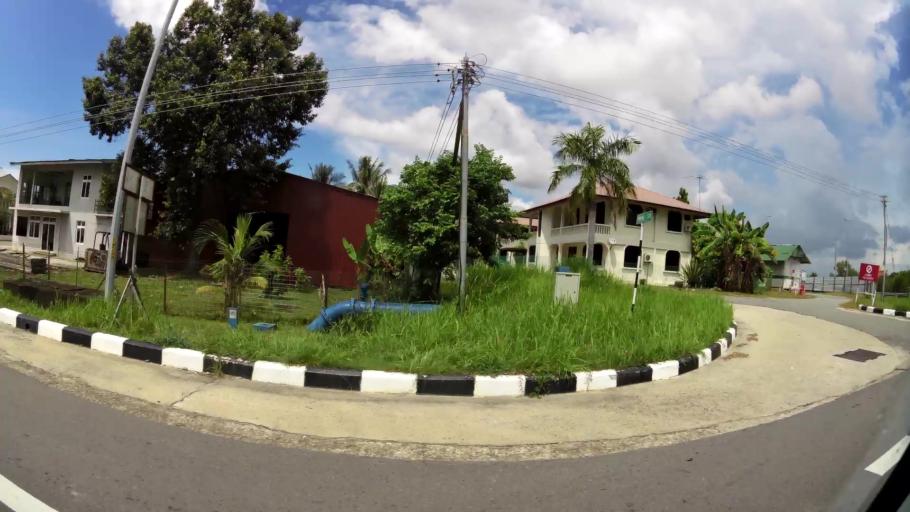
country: BN
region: Brunei and Muara
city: Bandar Seri Begawan
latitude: 4.9870
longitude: 114.9541
